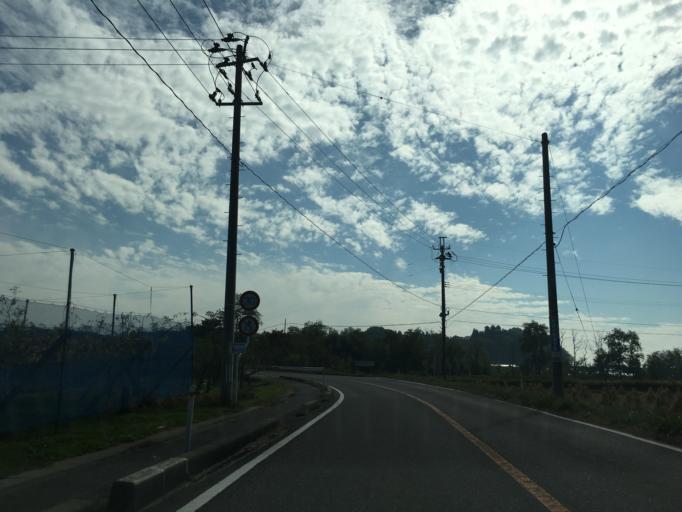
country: JP
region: Fukushima
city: Sukagawa
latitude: 37.2737
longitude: 140.4051
